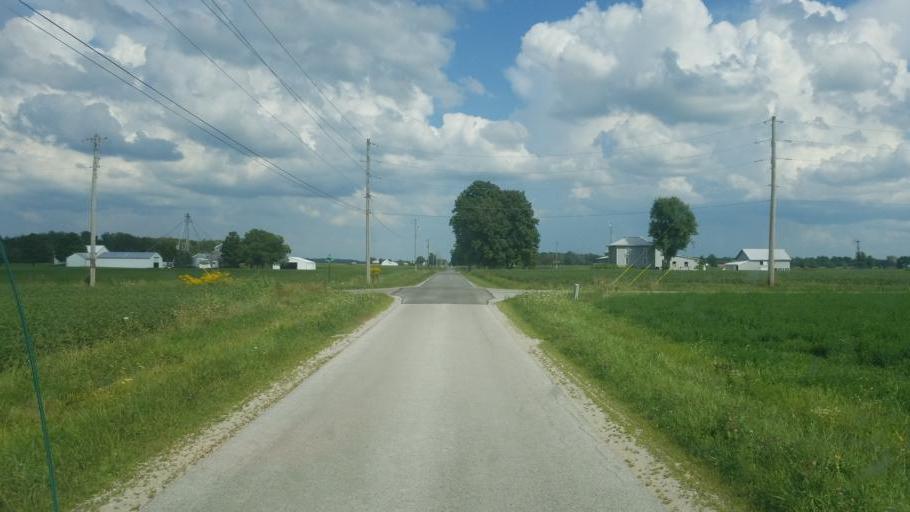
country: US
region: Ohio
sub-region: Huron County
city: Willard
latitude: 41.0082
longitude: -82.9013
